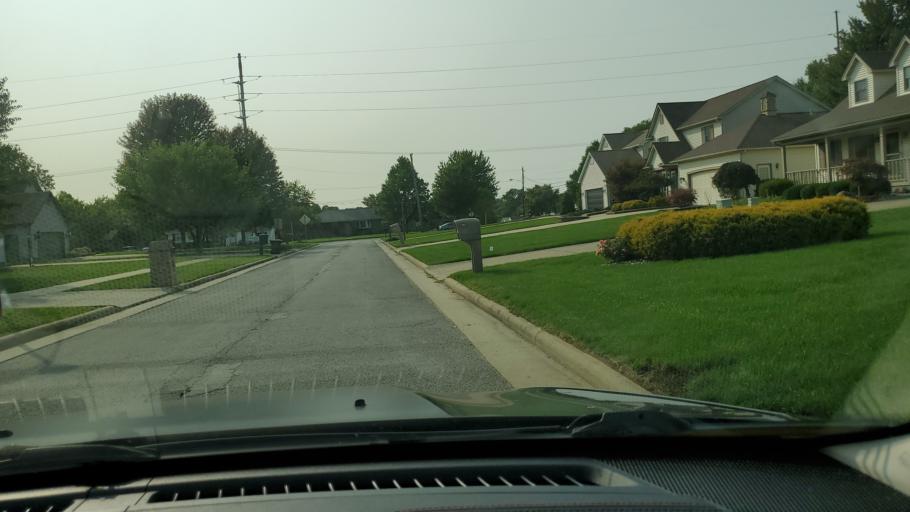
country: US
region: Ohio
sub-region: Mahoning County
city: Poland
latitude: 41.0369
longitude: -80.6199
